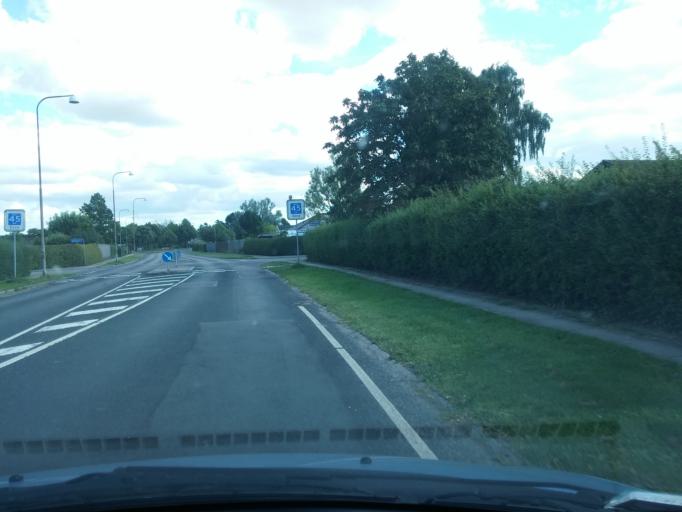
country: DK
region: South Denmark
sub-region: Odense Kommune
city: Bullerup
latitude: 55.4298
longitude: 10.4724
